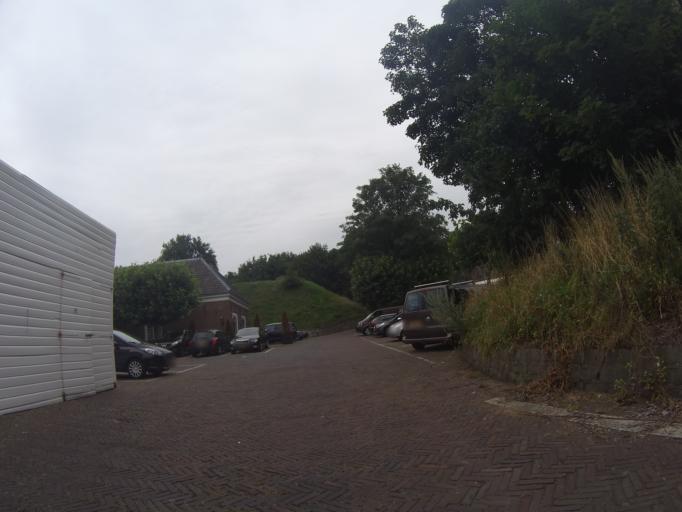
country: NL
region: North Holland
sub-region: Gemeente Naarden
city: Naarden
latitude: 52.2974
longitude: 5.1614
